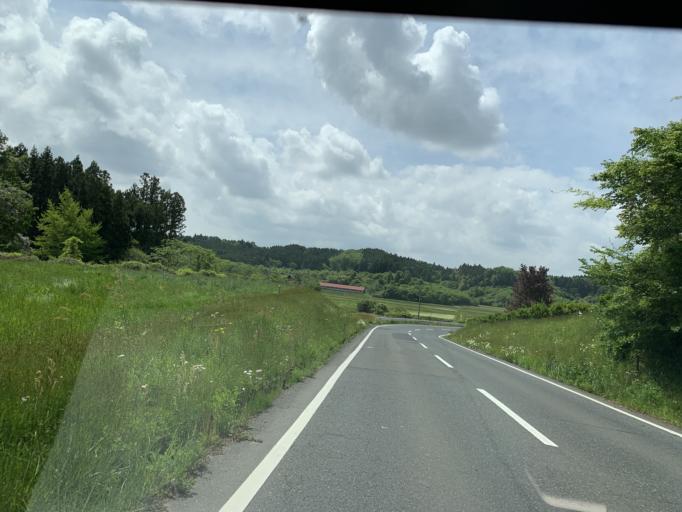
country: JP
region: Iwate
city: Ichinoseki
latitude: 38.7833
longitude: 141.0004
